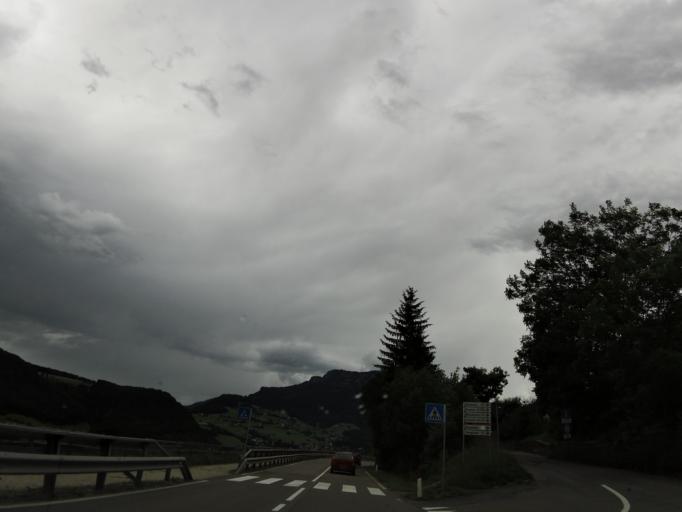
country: IT
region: Trentino-Alto Adige
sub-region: Bolzano
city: Siusi
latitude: 46.5344
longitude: 11.5285
